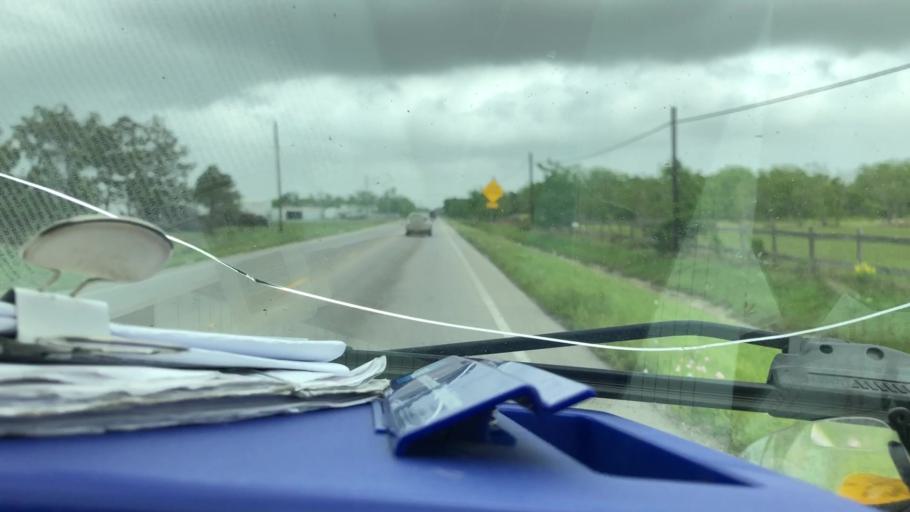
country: US
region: Texas
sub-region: Galveston County
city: Bacliff
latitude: 29.4791
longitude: -94.9705
